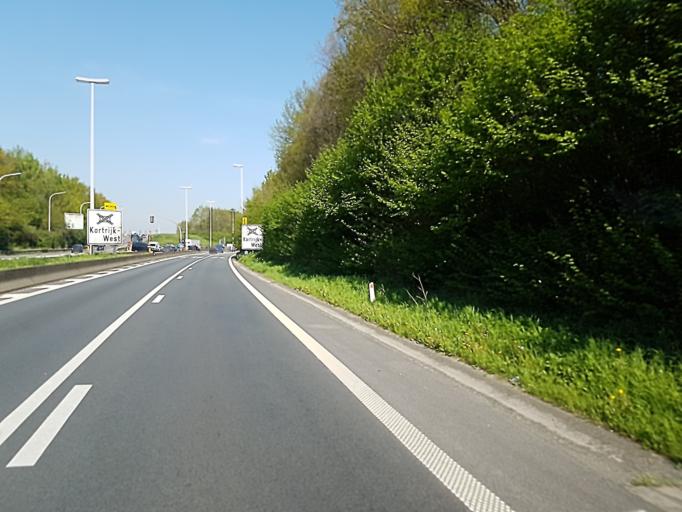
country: BE
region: Flanders
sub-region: Provincie West-Vlaanderen
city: Kortrijk
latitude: 50.8265
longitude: 3.2173
